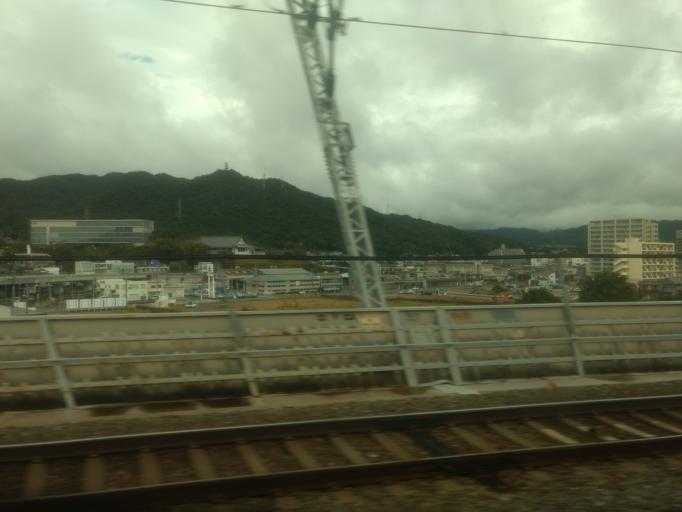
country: JP
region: Yamaguchi
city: Ogori-shimogo
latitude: 34.0904
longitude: 131.3926
